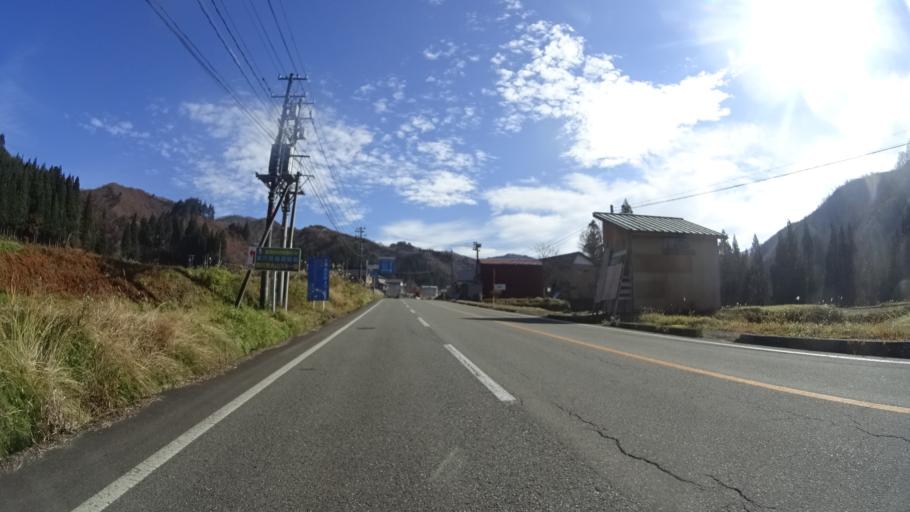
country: JP
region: Niigata
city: Muikamachi
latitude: 37.2053
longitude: 139.0699
